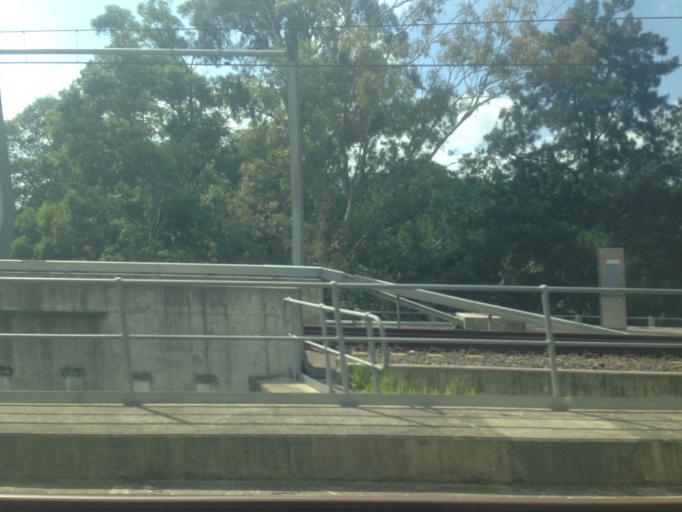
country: AU
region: New South Wales
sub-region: Willoughby
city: Chatswood
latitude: -33.7988
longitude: 151.1810
